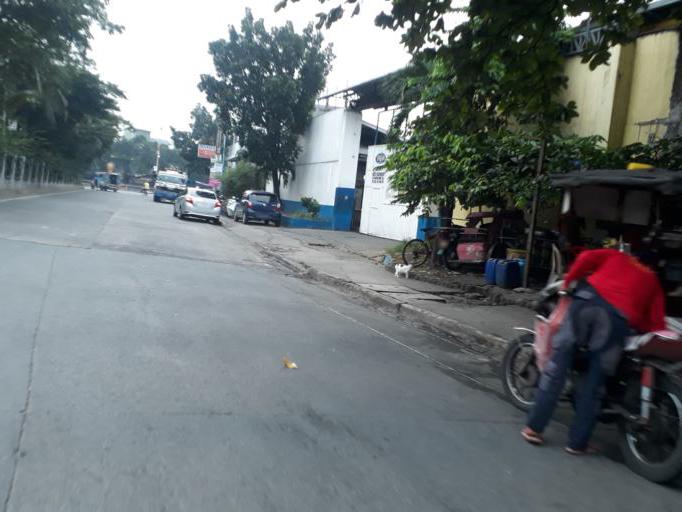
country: PH
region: Metro Manila
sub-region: Caloocan City
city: Niugan
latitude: 14.6586
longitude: 120.9617
